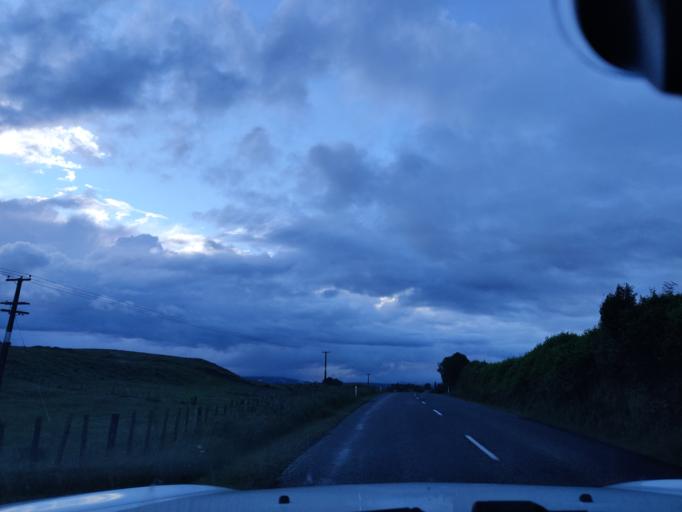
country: NZ
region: Waikato
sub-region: South Waikato District
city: Tokoroa
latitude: -38.2178
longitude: 175.8304
